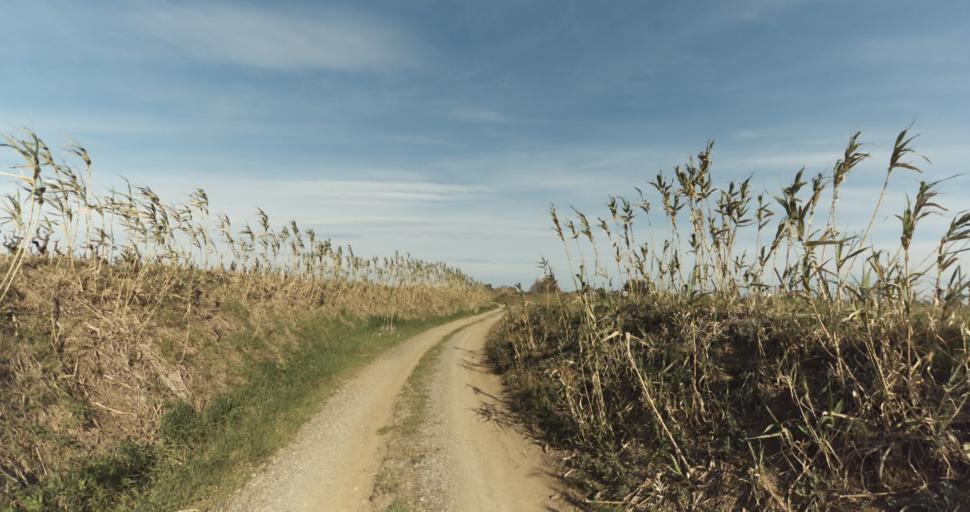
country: FR
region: Languedoc-Roussillon
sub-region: Departement de l'Herault
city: Marseillan
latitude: 43.3680
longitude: 3.5127
